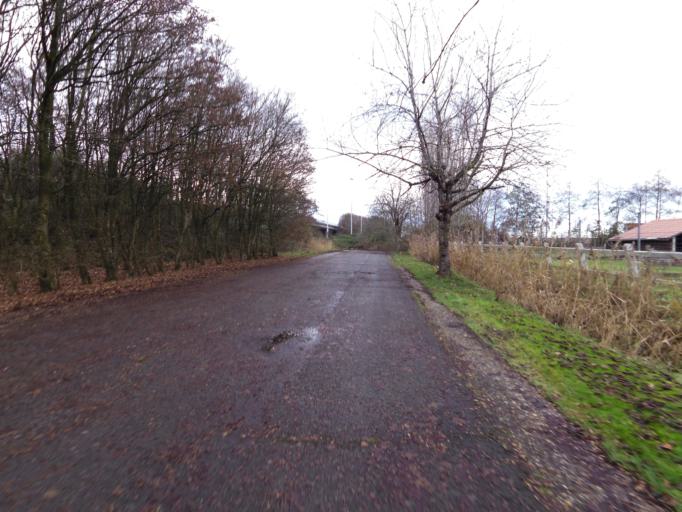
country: BE
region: Flanders
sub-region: Provincie West-Vlaanderen
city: Middelkerke
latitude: 51.1406
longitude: 2.8617
